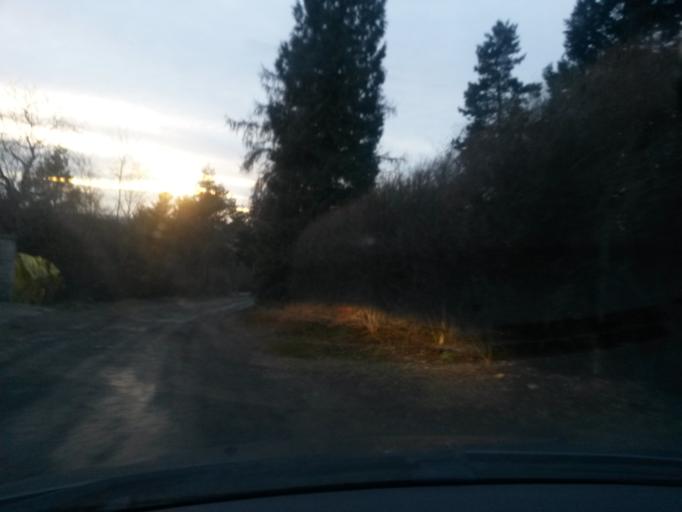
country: CZ
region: Central Bohemia
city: Psary
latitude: 49.9457
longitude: 14.5330
